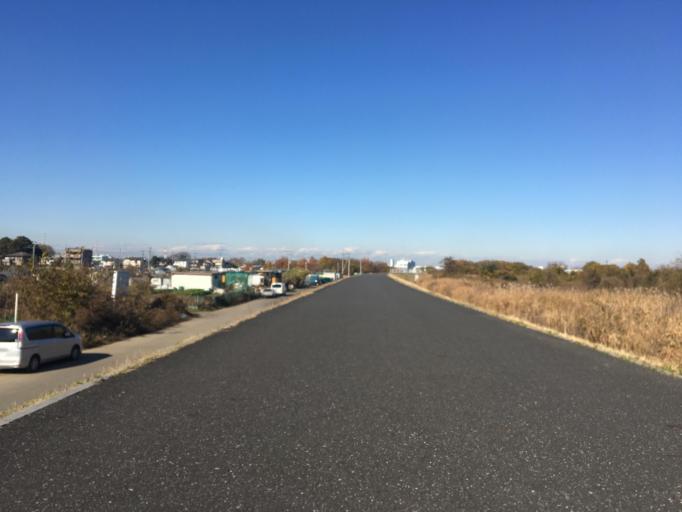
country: JP
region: Saitama
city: Yashio-shi
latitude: 35.8312
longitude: 139.8437
